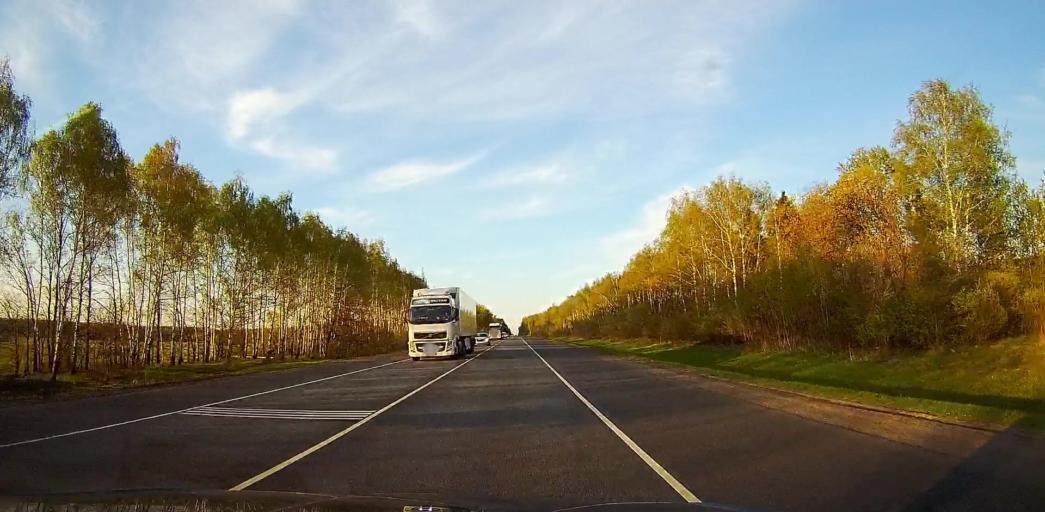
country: RU
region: Moskovskaya
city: Meshcherino
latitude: 55.2438
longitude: 38.4345
